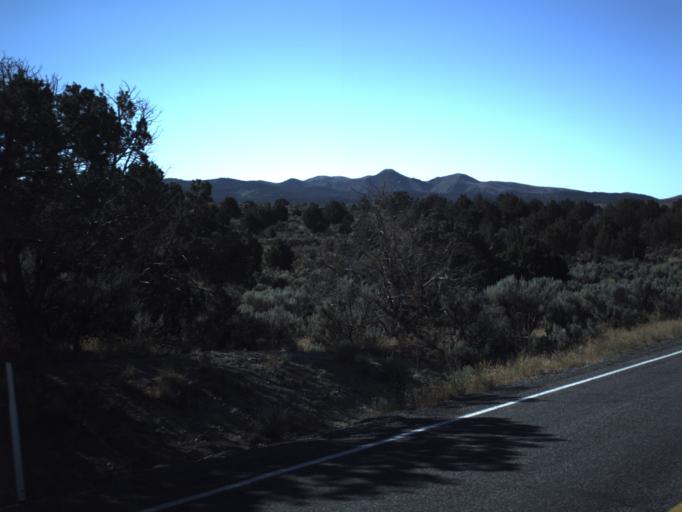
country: US
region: Utah
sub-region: Juab County
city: Mona
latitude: 39.8199
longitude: -112.1414
